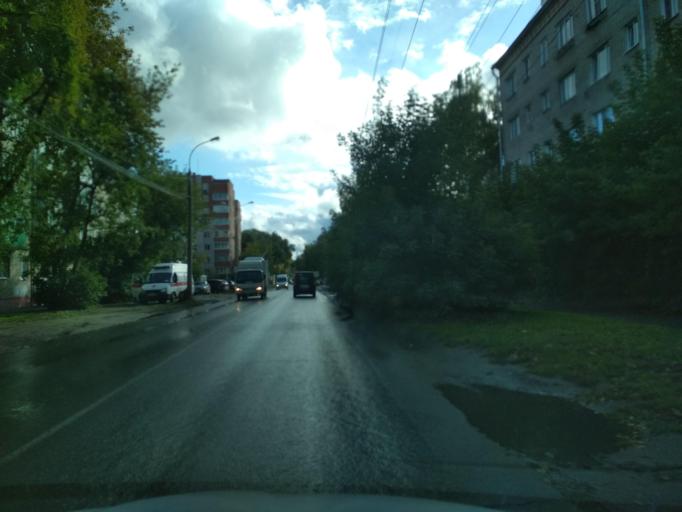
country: RU
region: Tomsk
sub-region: Tomskiy Rayon
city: Tomsk
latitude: 56.4711
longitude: 84.9757
